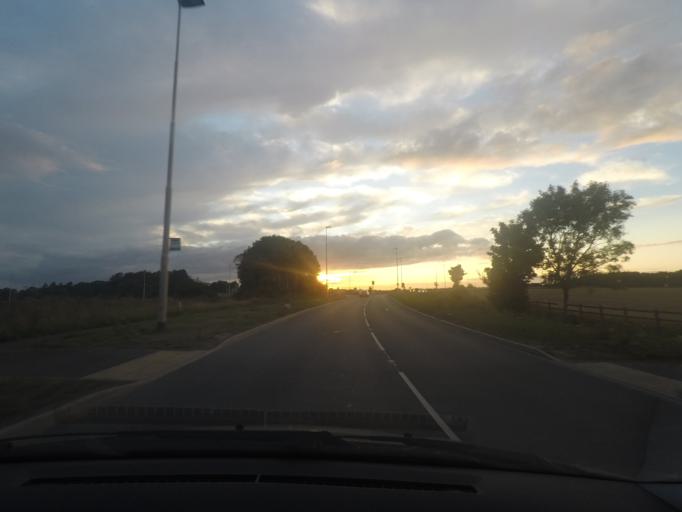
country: GB
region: England
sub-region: North Lincolnshire
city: Barnetby le Wold
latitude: 53.5822
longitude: -0.4092
